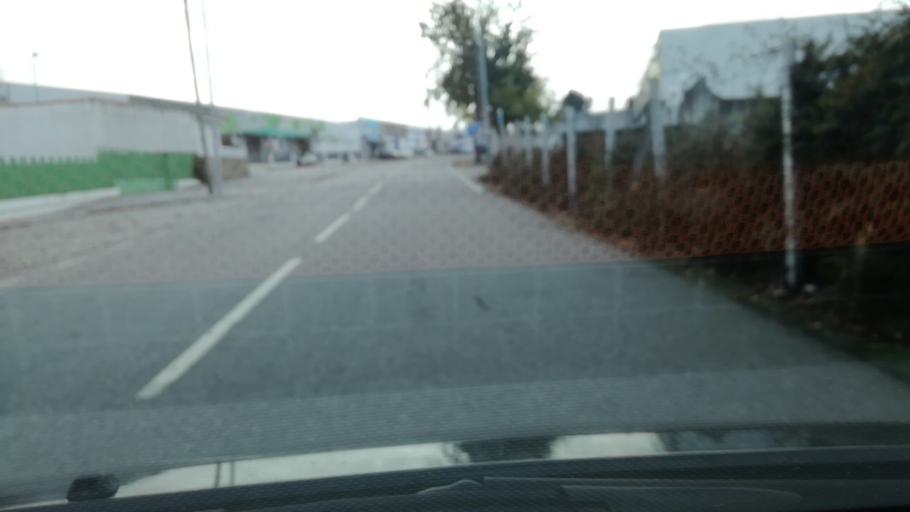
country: PT
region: Porto
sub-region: Maia
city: Gemunde
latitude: 41.2636
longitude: -8.6477
